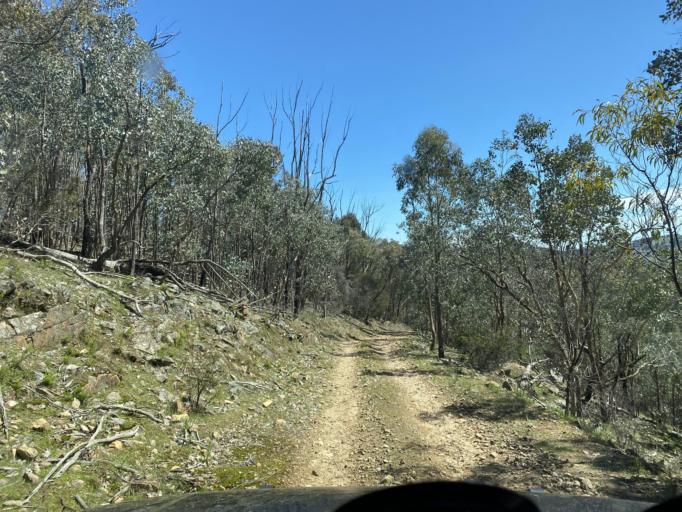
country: AU
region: Victoria
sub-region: Benalla
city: Benalla
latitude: -36.7202
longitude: 146.1824
